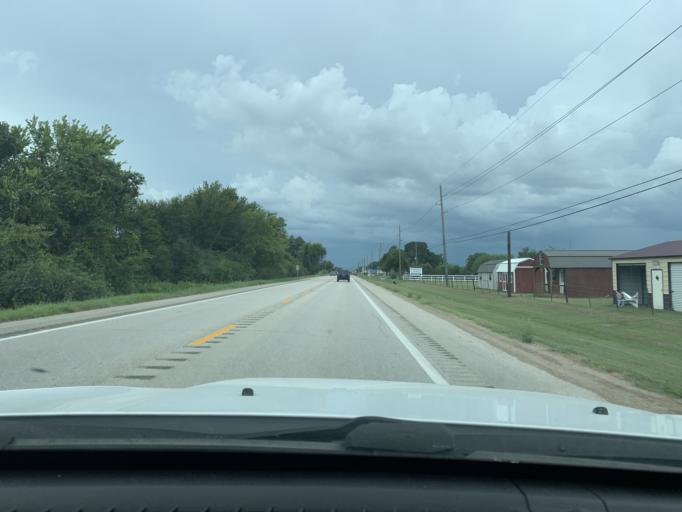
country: US
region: Texas
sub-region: Fort Bend County
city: Greatwood
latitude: 29.5397
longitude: -95.7186
